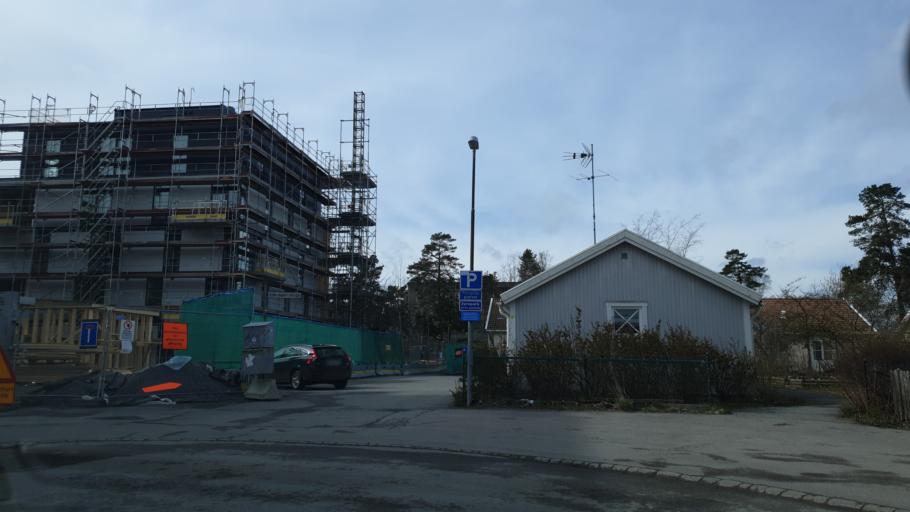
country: SE
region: Stockholm
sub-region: Nacka Kommun
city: Boo
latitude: 59.3279
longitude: 18.2548
